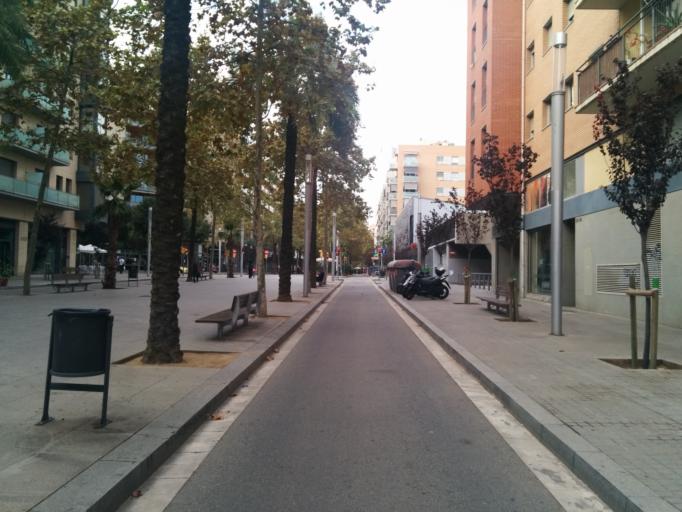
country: ES
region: Catalonia
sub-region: Provincia de Barcelona
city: Sant Marti
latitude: 41.4037
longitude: 2.1979
